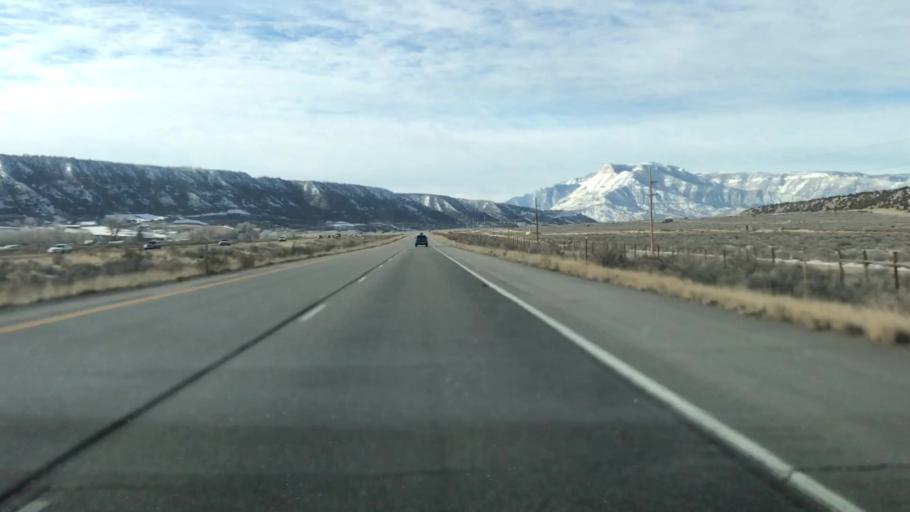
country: US
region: Colorado
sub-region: Garfield County
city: Battlement Mesa
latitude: 39.4844
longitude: -107.9643
